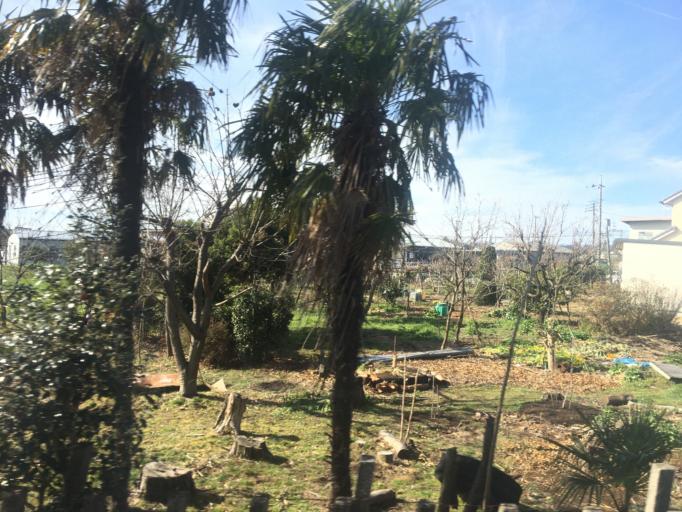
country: JP
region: Saitama
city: Sakado
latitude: 35.9322
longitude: 139.4312
